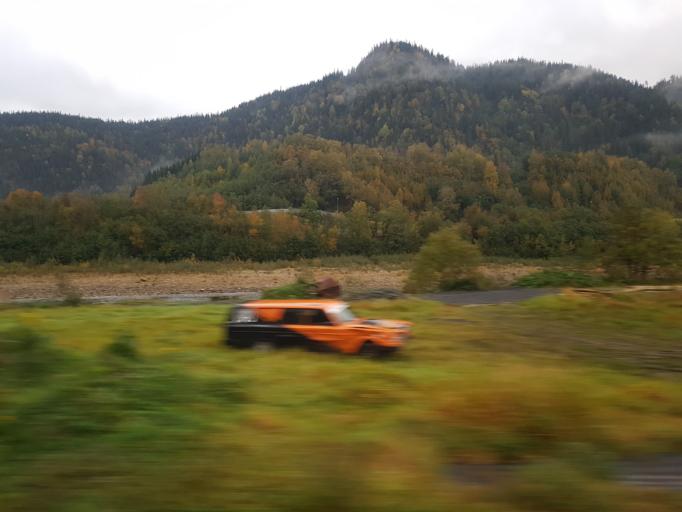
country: NO
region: Sor-Trondelag
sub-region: Midtre Gauldal
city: Storen
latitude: 63.0723
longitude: 10.2714
